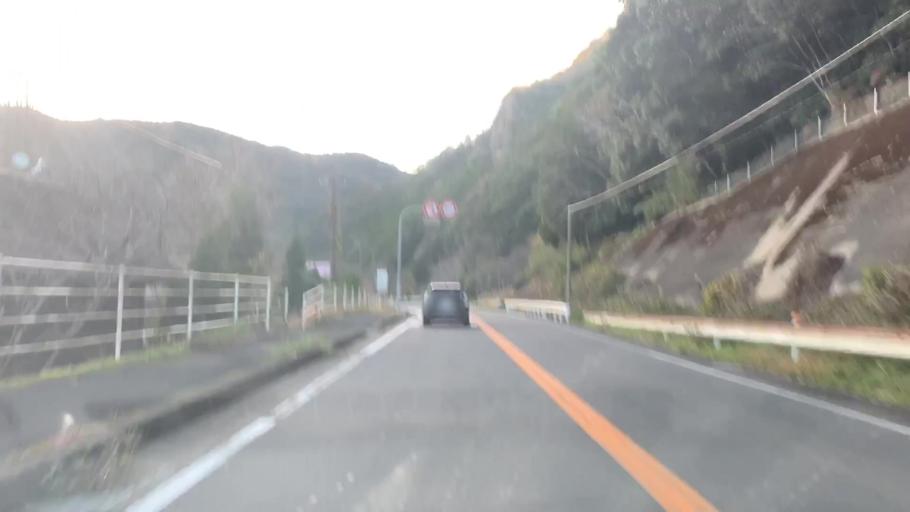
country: JP
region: Saga Prefecture
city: Karatsu
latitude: 33.3368
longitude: 129.9756
